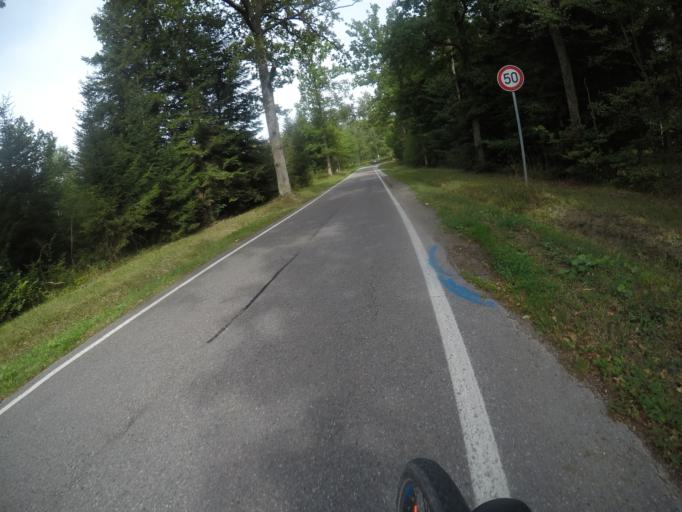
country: DE
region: Baden-Wuerttemberg
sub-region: Karlsruhe Region
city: Eutingen
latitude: 48.8707
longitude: 8.7613
